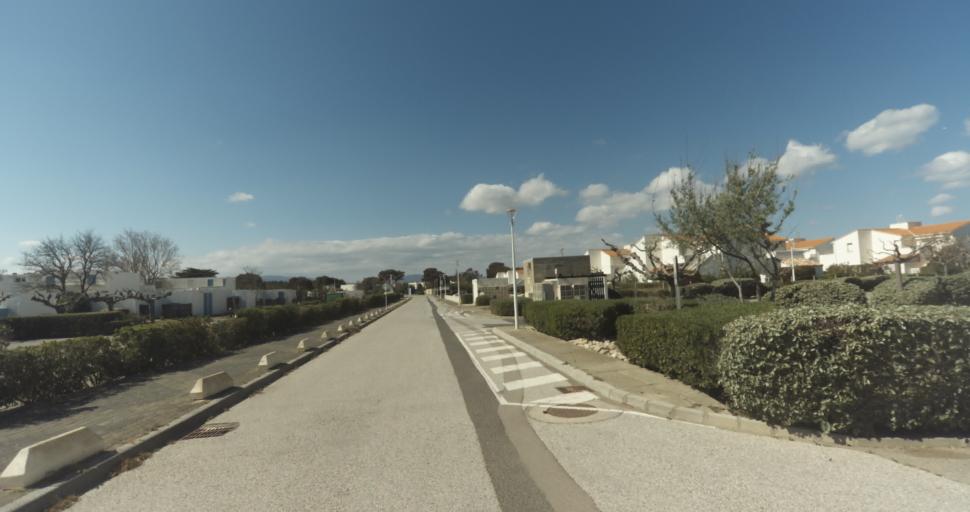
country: FR
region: Languedoc-Roussillon
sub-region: Departement de l'Aude
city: Leucate
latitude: 42.8500
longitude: 3.0424
